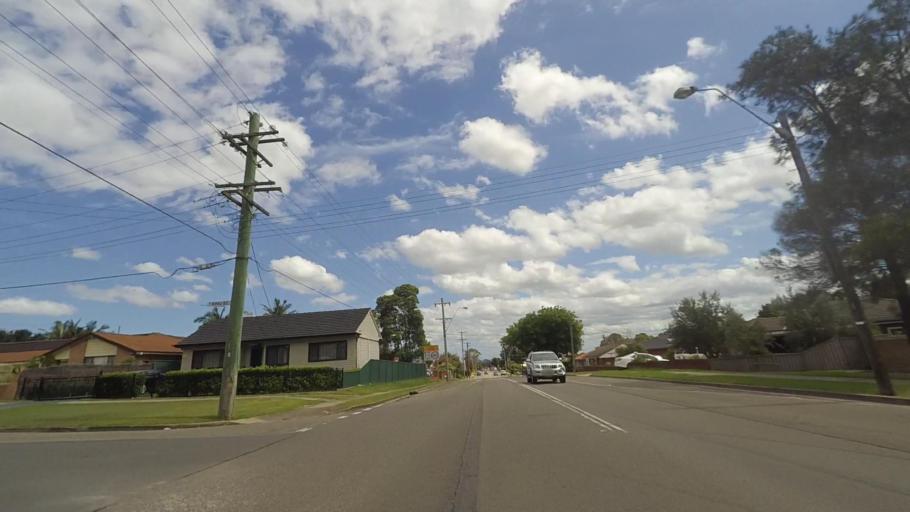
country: AU
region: New South Wales
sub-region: Holroyd
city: Guildford West
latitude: -33.8458
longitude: 150.9624
